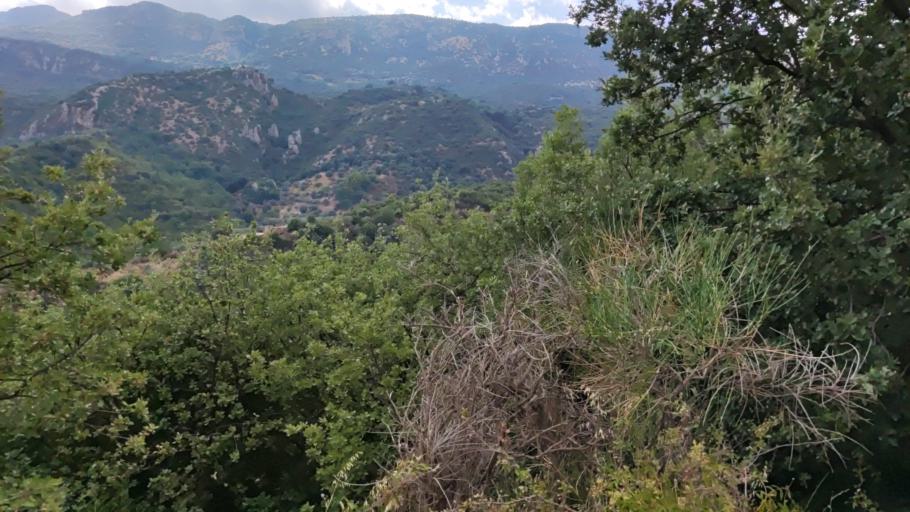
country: IT
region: Calabria
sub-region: Provincia di Reggio Calabria
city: Pazzano
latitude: 38.4471
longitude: 16.4482
